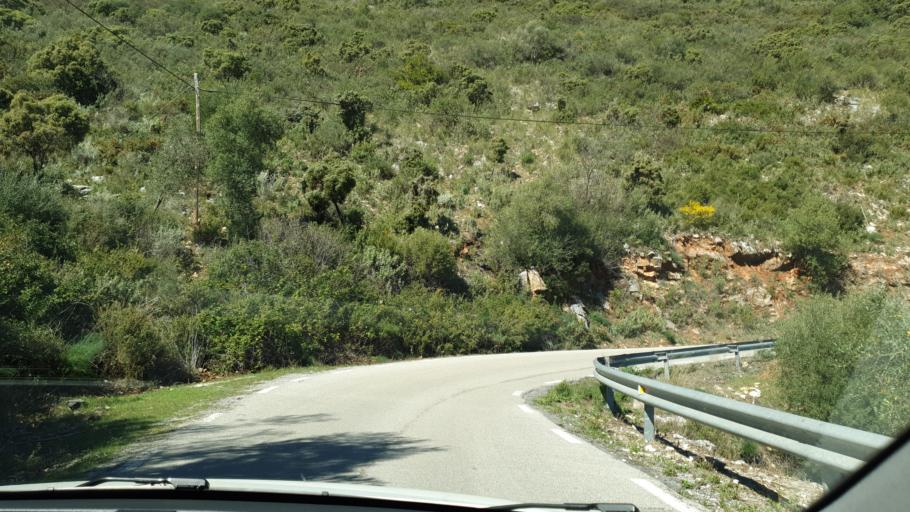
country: ES
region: Andalusia
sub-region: Provincia de Malaga
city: Ojen
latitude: 36.5867
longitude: -4.8724
